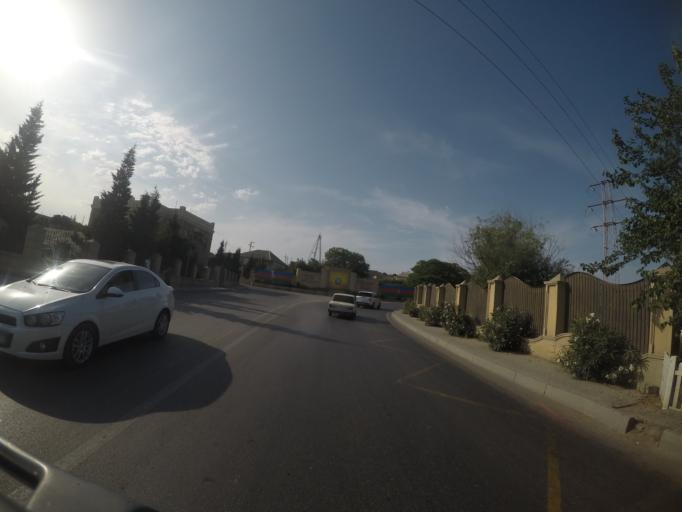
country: AZ
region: Baki
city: Binagadi
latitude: 40.4630
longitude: 49.8412
